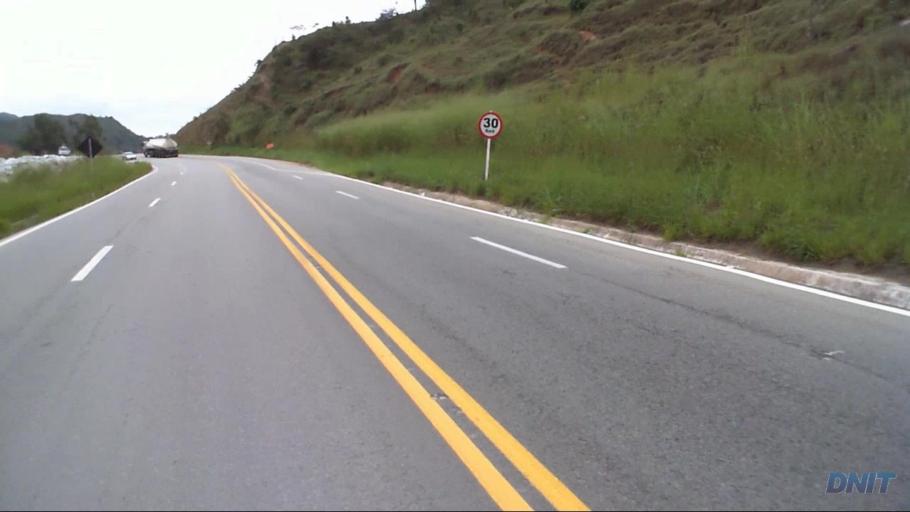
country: BR
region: Minas Gerais
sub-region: Nova Era
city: Nova Era
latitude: -19.6405
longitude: -42.9001
